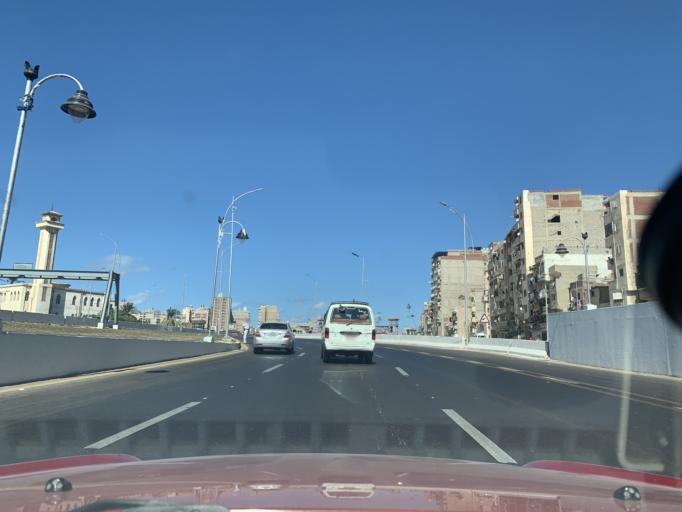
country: EG
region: Alexandria
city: Alexandria
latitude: 31.2181
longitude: 29.9640
